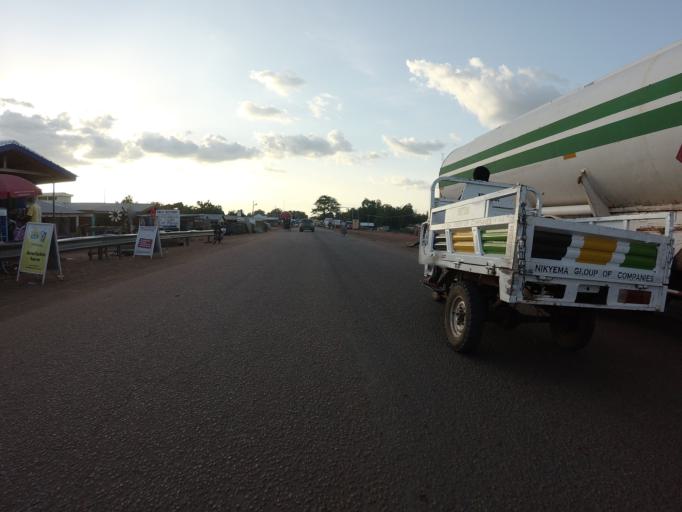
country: GH
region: Upper East
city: Navrongo
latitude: 10.9919
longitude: -1.1115
